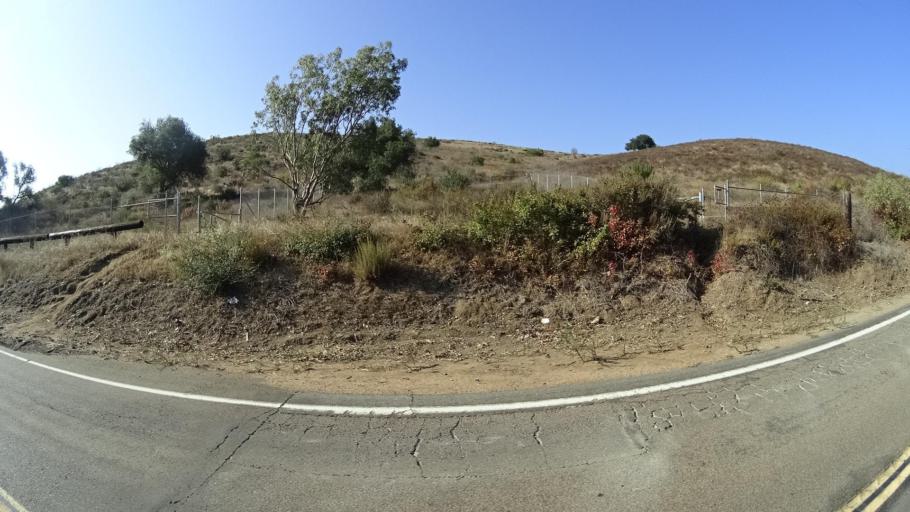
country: US
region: California
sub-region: San Diego County
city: Bonsall
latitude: 33.2896
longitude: -117.2303
